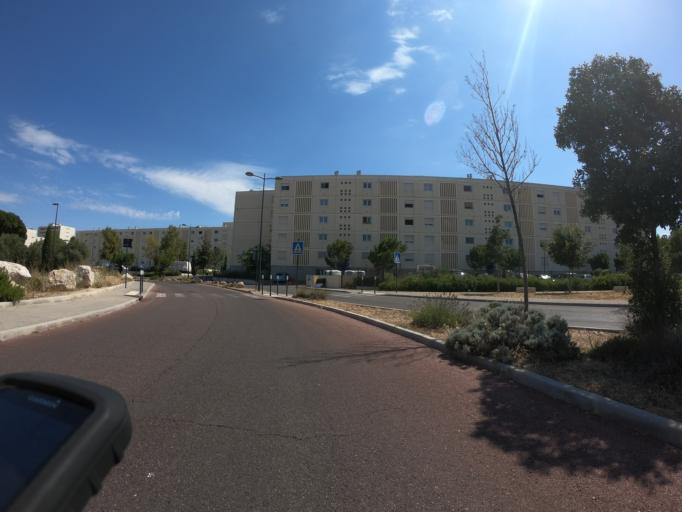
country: FR
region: Provence-Alpes-Cote d'Azur
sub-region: Departement du Var
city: Six-Fours-les-Plages
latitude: 43.1110
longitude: 5.8624
